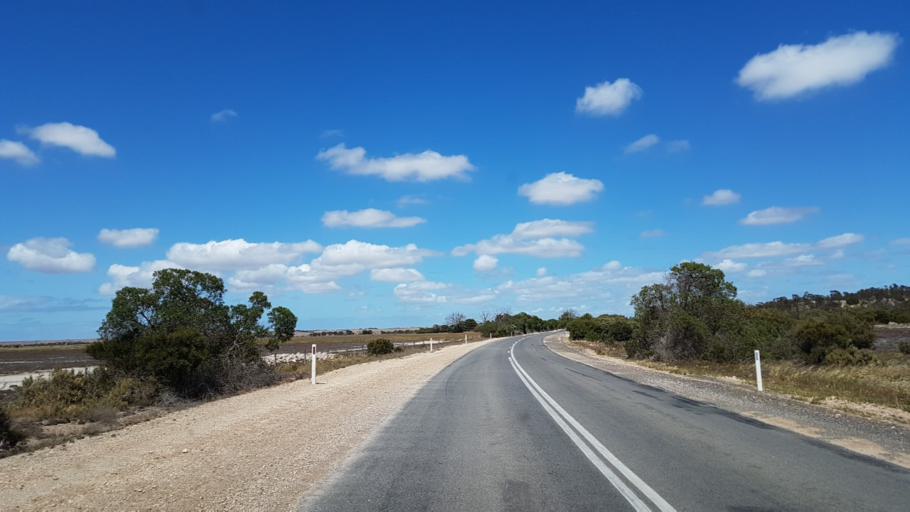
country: AU
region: South Australia
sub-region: Yorke Peninsula
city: Honiton
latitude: -34.9354
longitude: 137.4437
